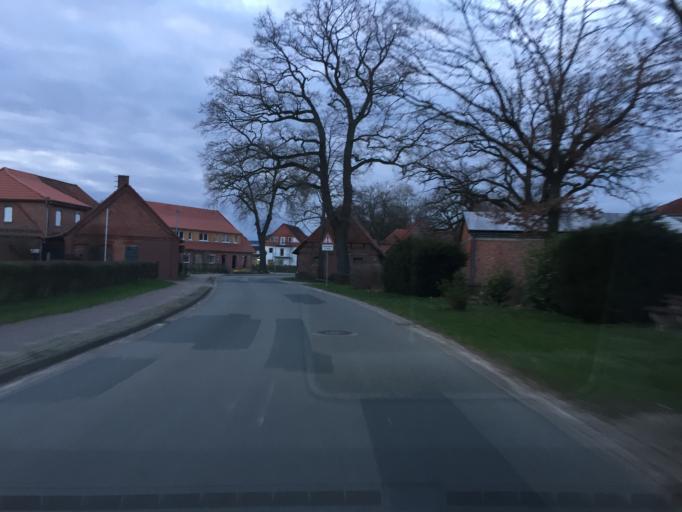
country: DE
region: Lower Saxony
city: Steimbke
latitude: 52.5945
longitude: 9.3993
